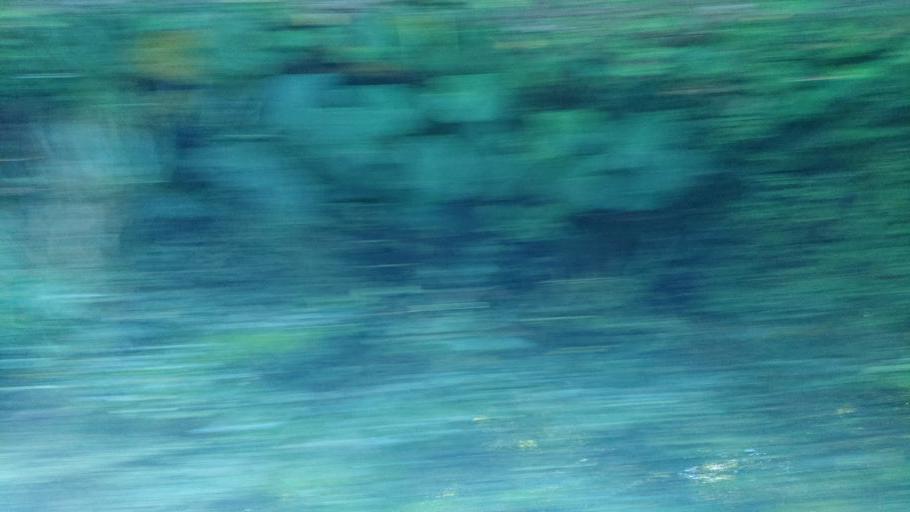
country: TW
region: Taiwan
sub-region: Chiayi
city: Jiayi Shi
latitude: 23.5330
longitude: 120.6295
